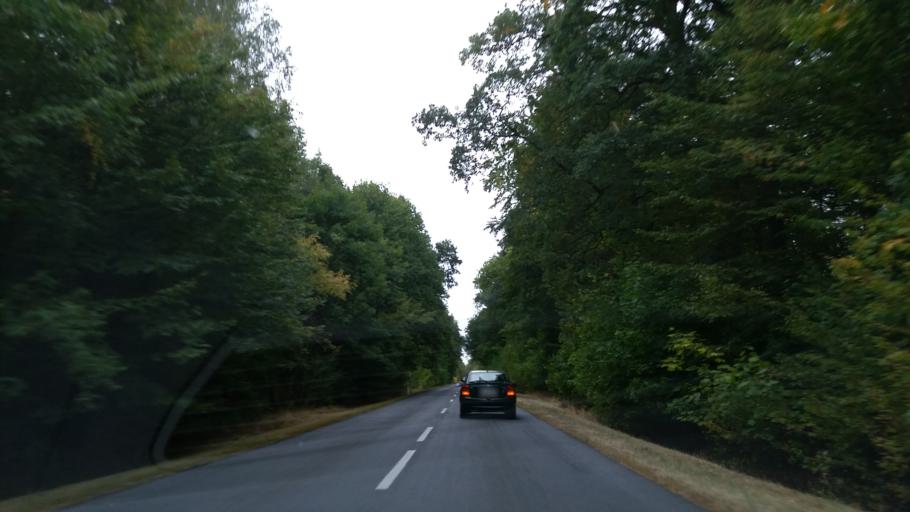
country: PL
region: Lubusz
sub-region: Powiat gorzowski
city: Klodawa
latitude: 52.8127
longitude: 15.2163
